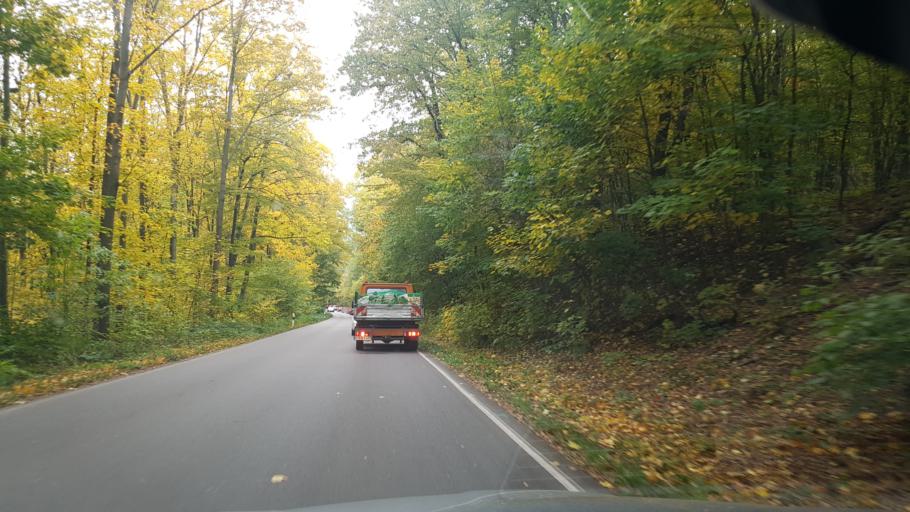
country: DE
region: Saxony
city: Struppen
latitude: 50.9237
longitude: 13.9762
